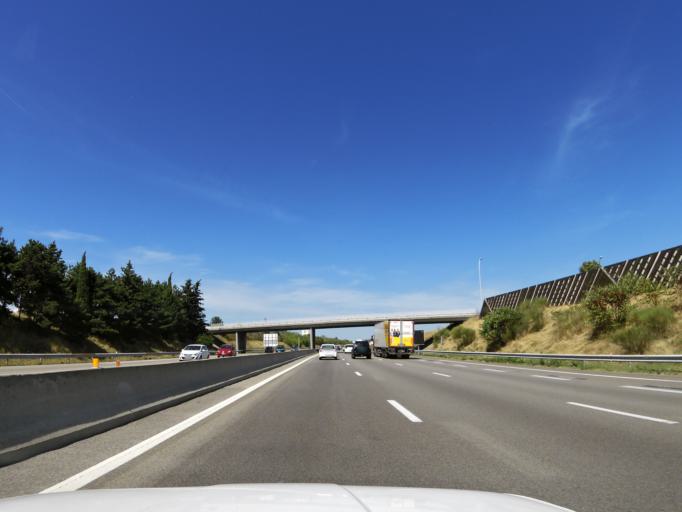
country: FR
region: Rhone-Alpes
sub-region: Departement de la Drome
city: Portes-les-Valence
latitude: 44.8704
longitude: 4.8649
